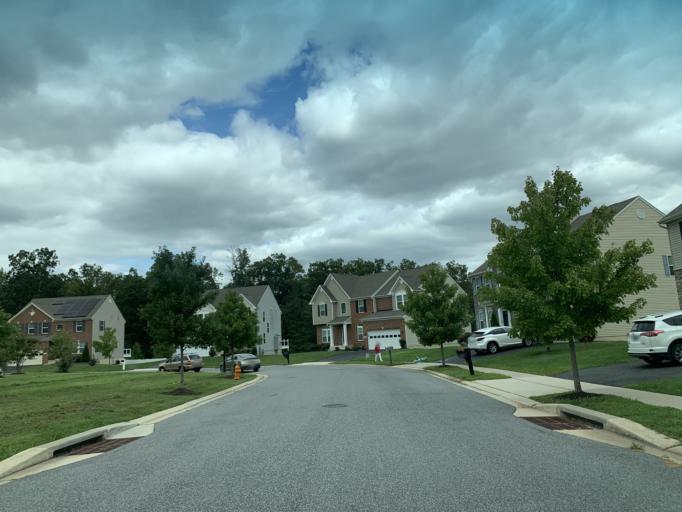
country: US
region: Maryland
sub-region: Baltimore County
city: White Marsh
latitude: 39.3926
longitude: -76.4192
